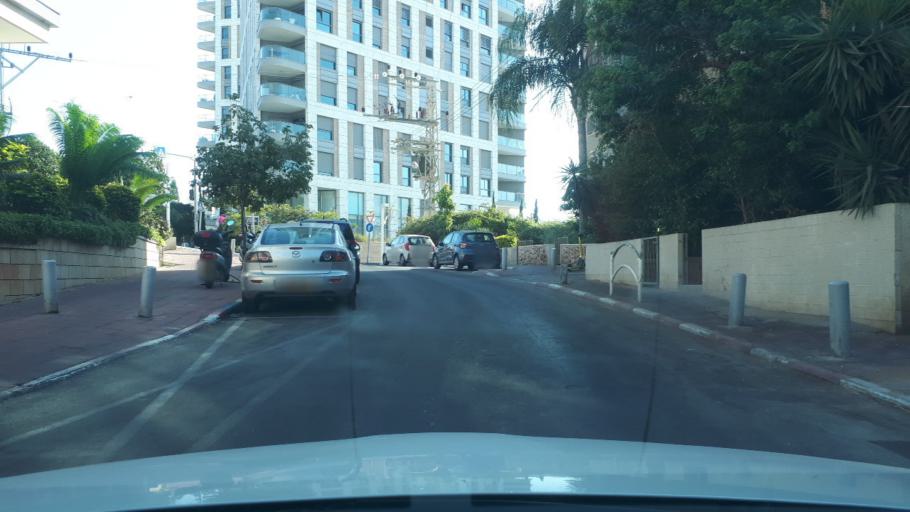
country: IL
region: Tel Aviv
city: Ramat Gan
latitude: 32.0799
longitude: 34.8115
